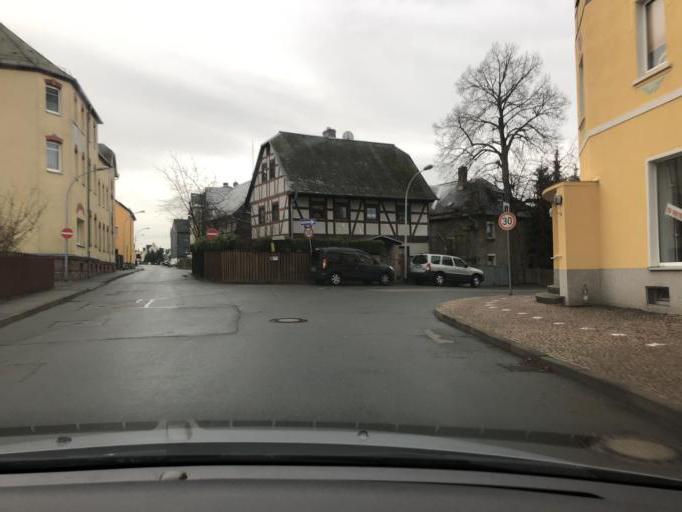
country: DE
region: Saxony
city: Limbach-Oberfrohna
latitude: 50.8519
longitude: 12.7292
